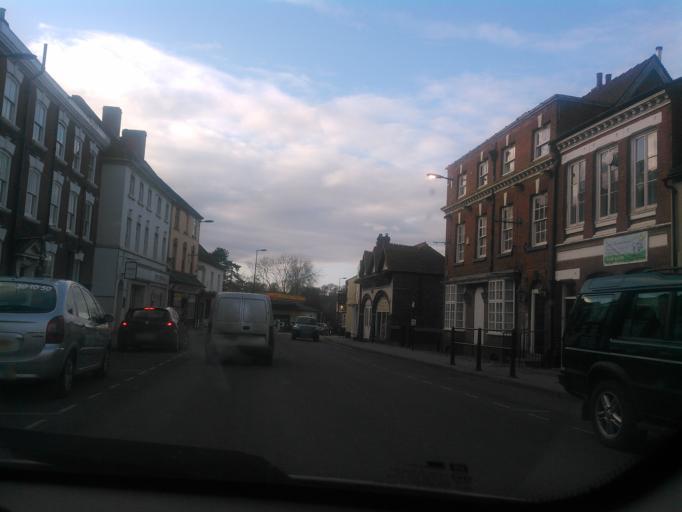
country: GB
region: England
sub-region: Telford and Wrekin
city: Newport
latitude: 52.7705
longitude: -2.3809
